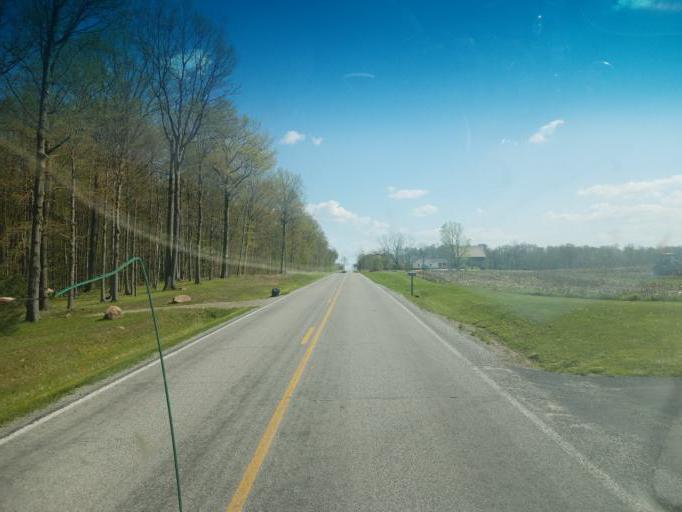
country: US
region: Ohio
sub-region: Medina County
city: Westfield Center
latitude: 40.9713
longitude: -81.9578
